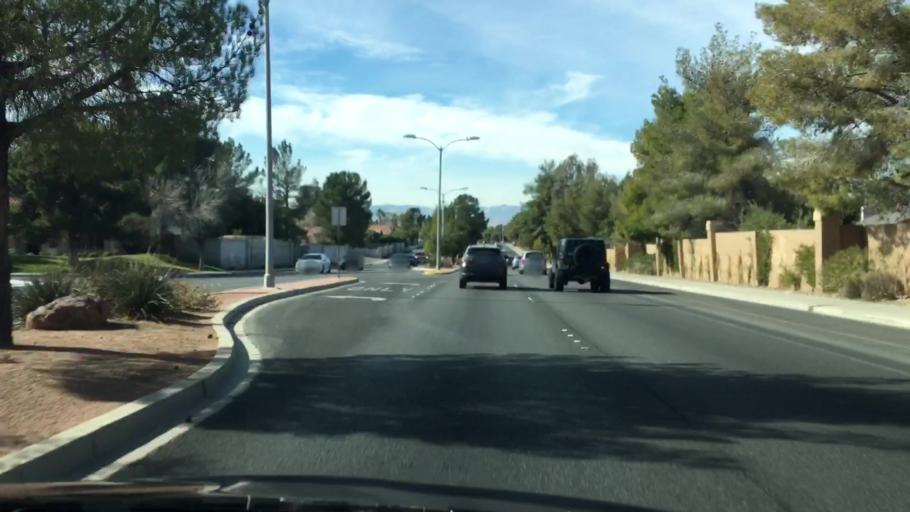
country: US
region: Nevada
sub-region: Clark County
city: Whitney
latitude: 36.0570
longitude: -115.0956
